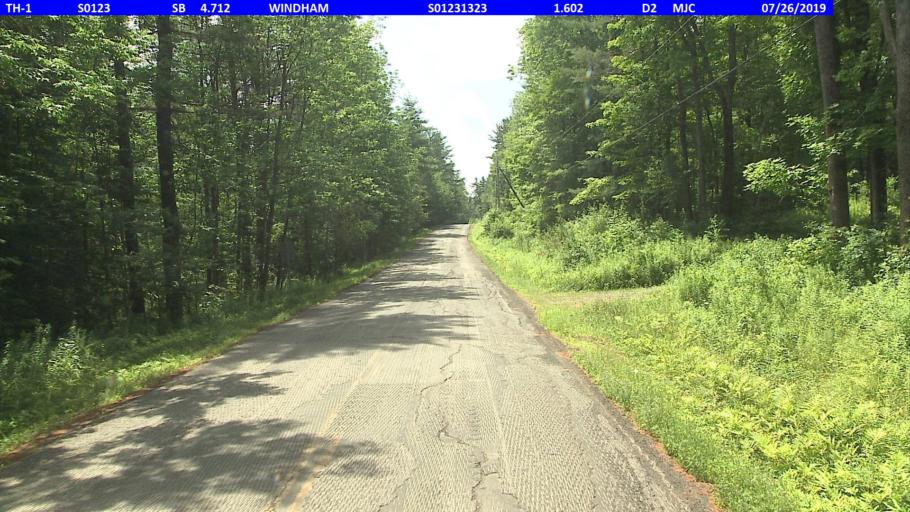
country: US
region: Vermont
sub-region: Windsor County
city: Chester
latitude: 43.1477
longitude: -72.7208
